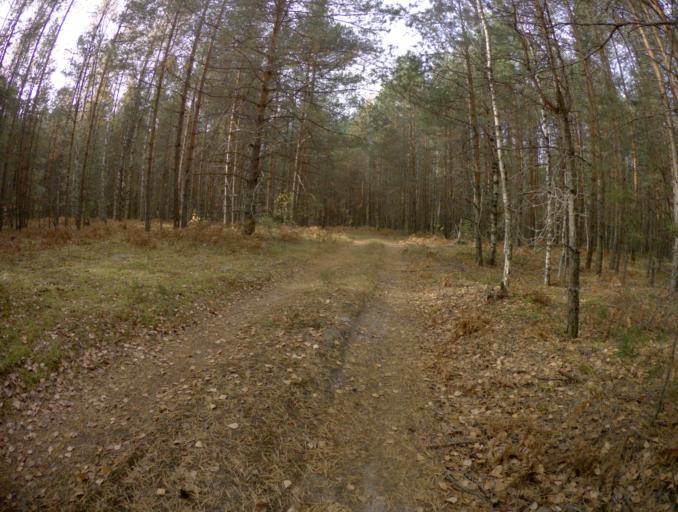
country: RU
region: Vladimir
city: Vorsha
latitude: 55.9553
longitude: 40.1370
